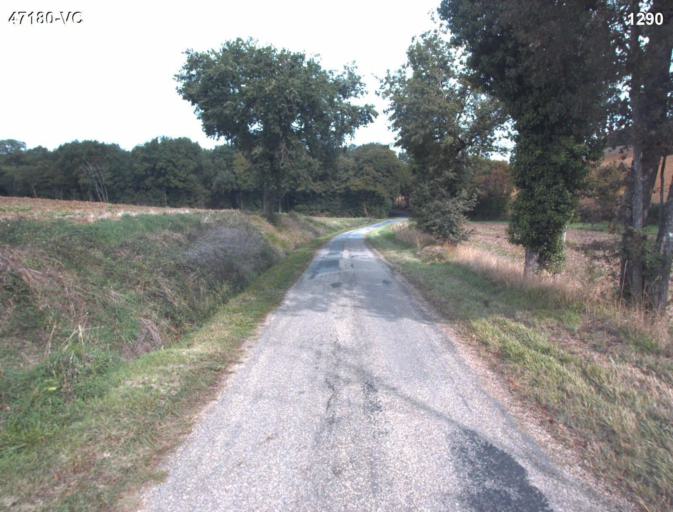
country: FR
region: Aquitaine
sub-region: Departement du Lot-et-Garonne
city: Sainte-Colombe-en-Bruilhois
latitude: 44.1791
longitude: 0.4410
